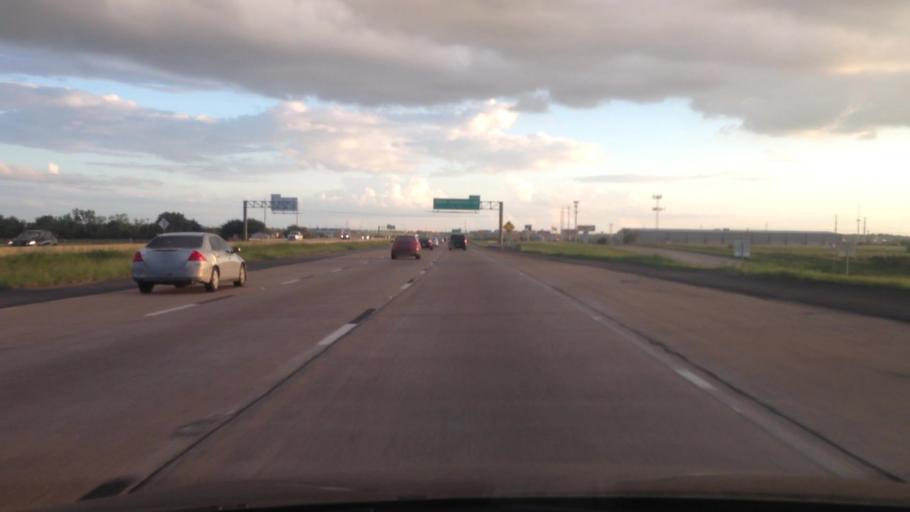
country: US
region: Texas
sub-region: Tarrant County
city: White Settlement
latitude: 32.7728
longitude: -97.4755
